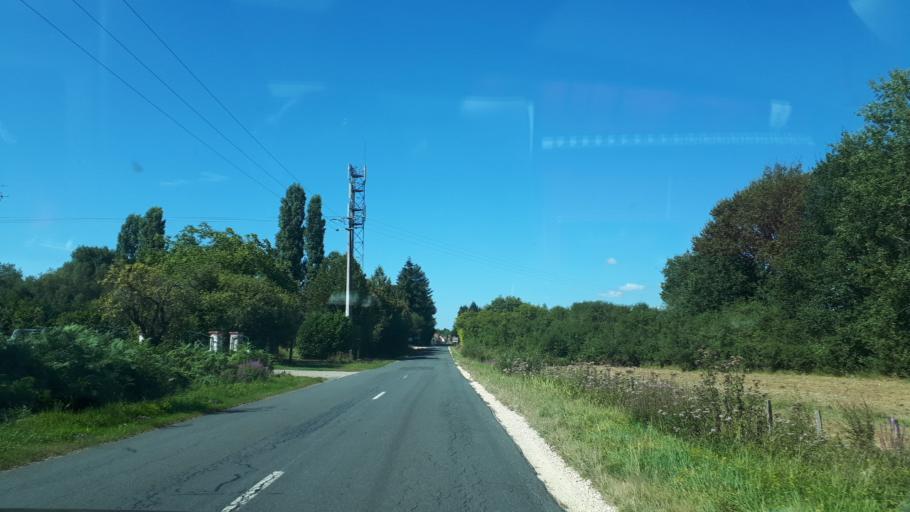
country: FR
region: Centre
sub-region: Departement du Cher
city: Brinon-sur-Sauldre
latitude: 47.6468
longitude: 2.1731
